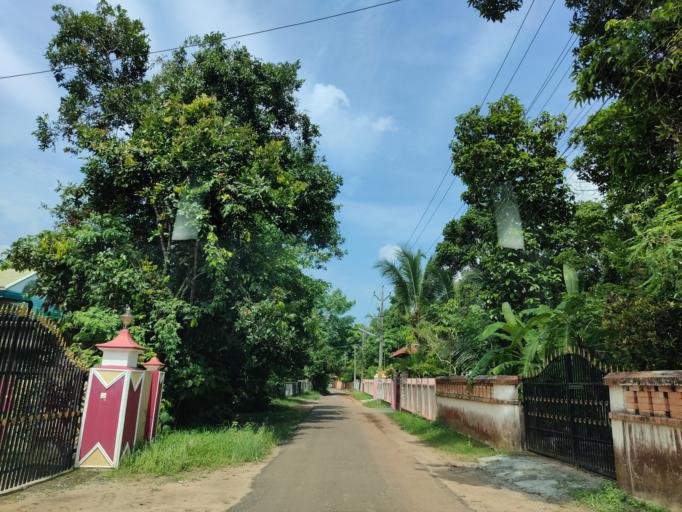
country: IN
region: Kerala
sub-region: Alappuzha
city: Mavelikara
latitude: 9.2607
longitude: 76.5597
